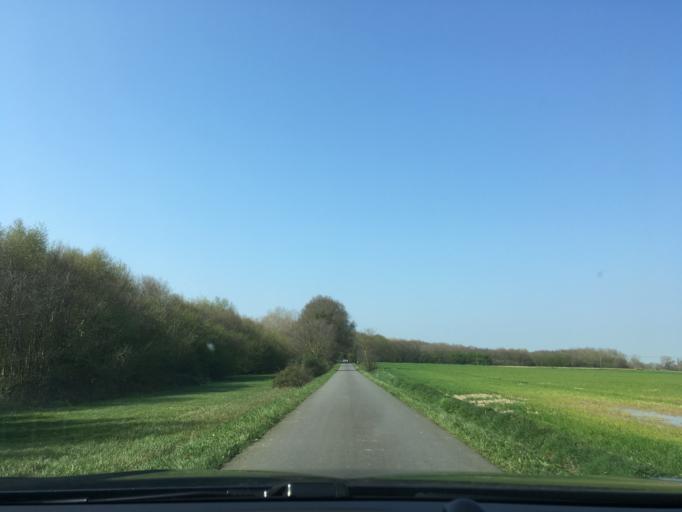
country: BE
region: Flanders
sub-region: Provincie West-Vlaanderen
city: Lichtervelde
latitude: 51.0019
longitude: 3.1547
